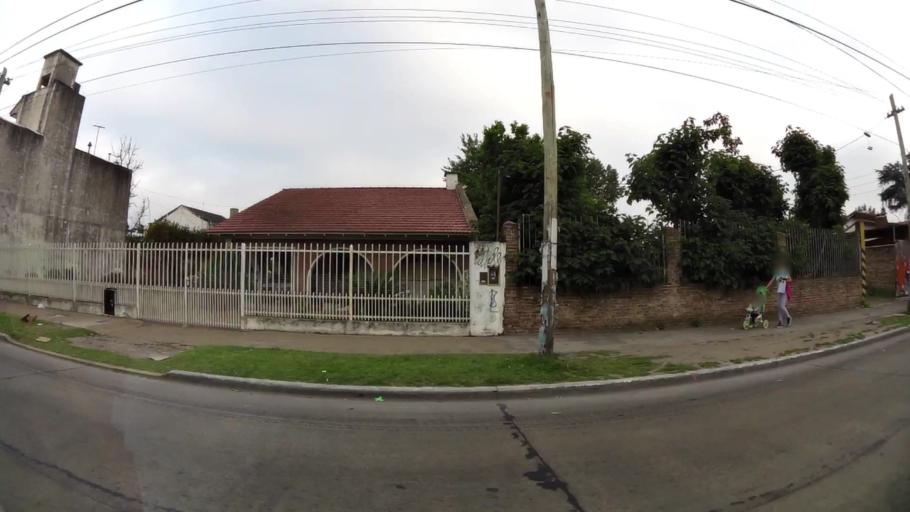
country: AR
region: Buenos Aires
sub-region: Partido de Moron
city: Moron
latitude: -34.6681
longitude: -58.6027
